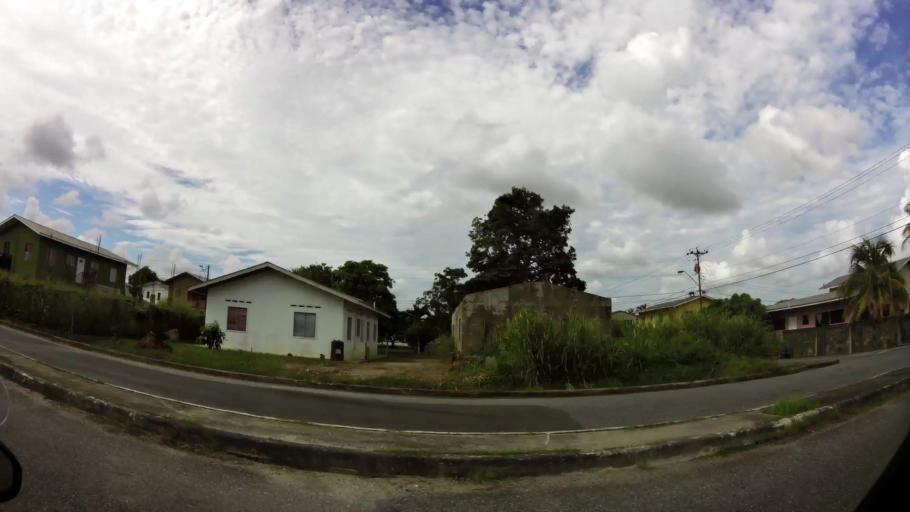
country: TT
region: Chaguanas
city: Chaguanas
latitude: 10.5101
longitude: -61.3953
